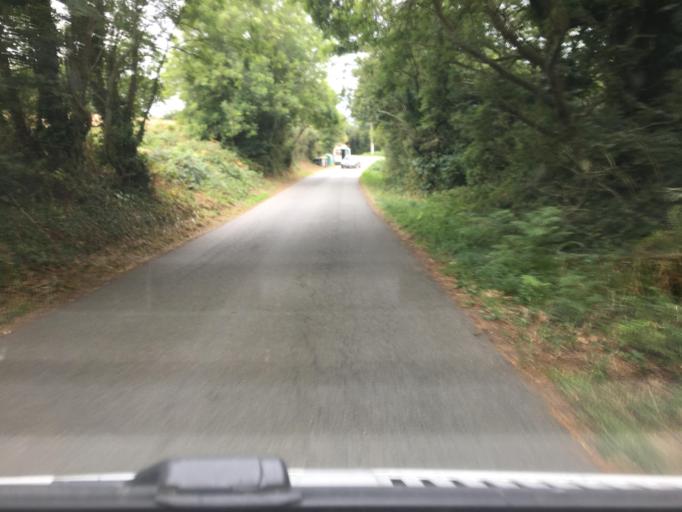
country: FR
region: Brittany
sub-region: Departement du Finistere
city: Beuzec-Cap-Sizun
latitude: 48.0790
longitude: -4.4771
